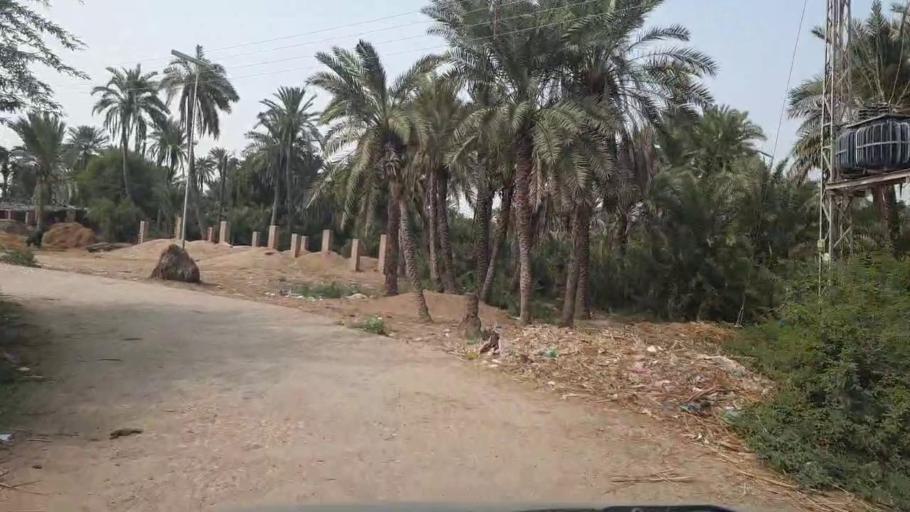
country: PK
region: Sindh
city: Tando Muhammad Khan
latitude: 25.1152
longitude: 68.3671
